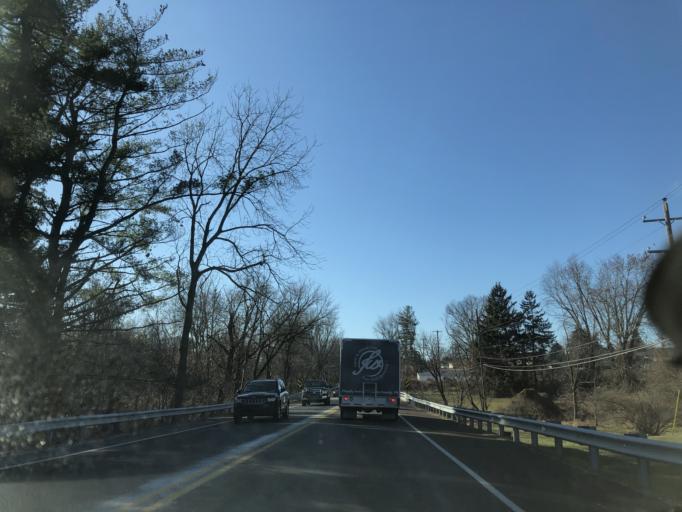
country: US
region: Pennsylvania
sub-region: Bucks County
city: Hulmeville
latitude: 40.1583
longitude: -74.8908
